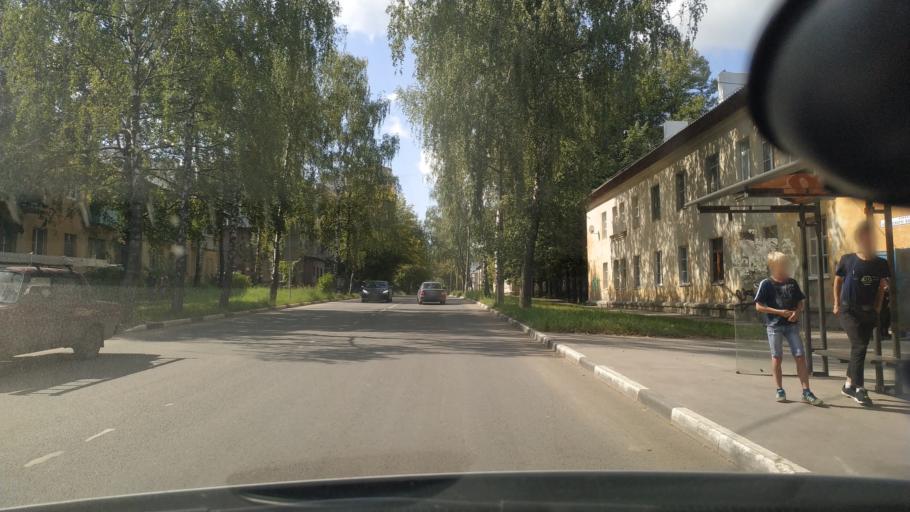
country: RU
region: Rjazan
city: Ryazan'
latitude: 54.6124
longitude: 39.7064
